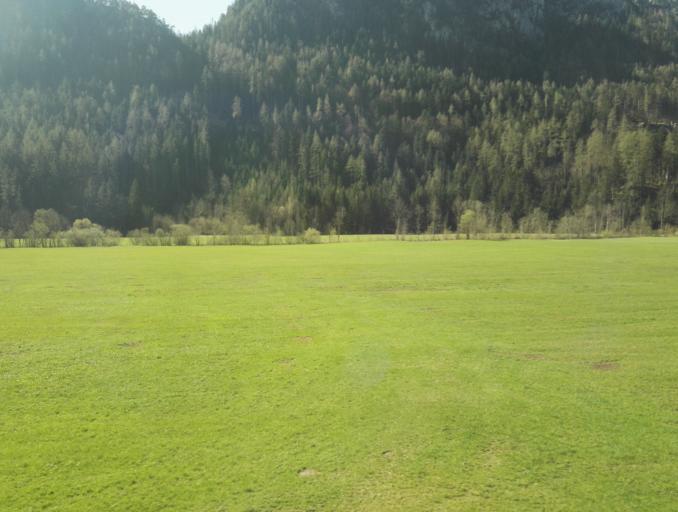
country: AT
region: Salzburg
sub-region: Politischer Bezirk Sankt Johann im Pongau
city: Forstau
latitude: 47.3977
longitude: 13.5310
